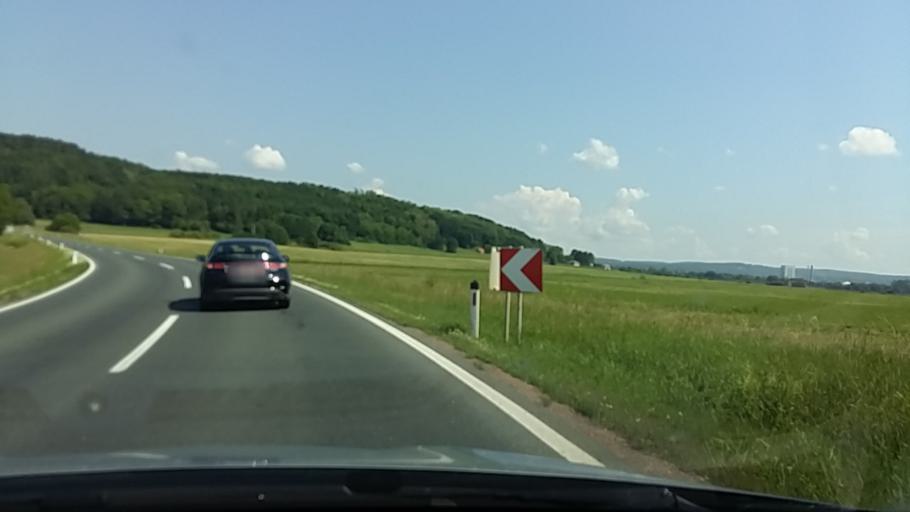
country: AT
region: Burgenland
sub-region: Politischer Bezirk Jennersdorf
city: Mogersdorf
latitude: 46.9525
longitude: 16.2447
